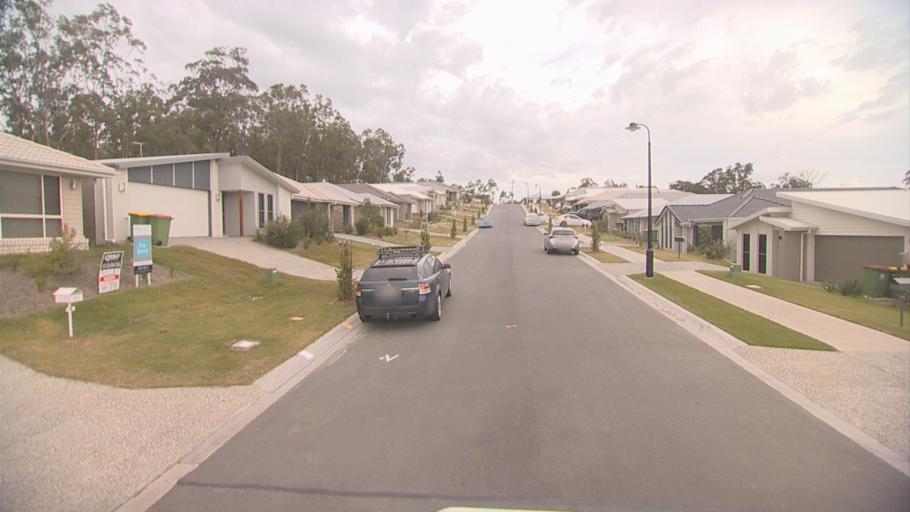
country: AU
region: Queensland
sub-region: Logan
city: Windaroo
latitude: -27.7240
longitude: 153.1647
